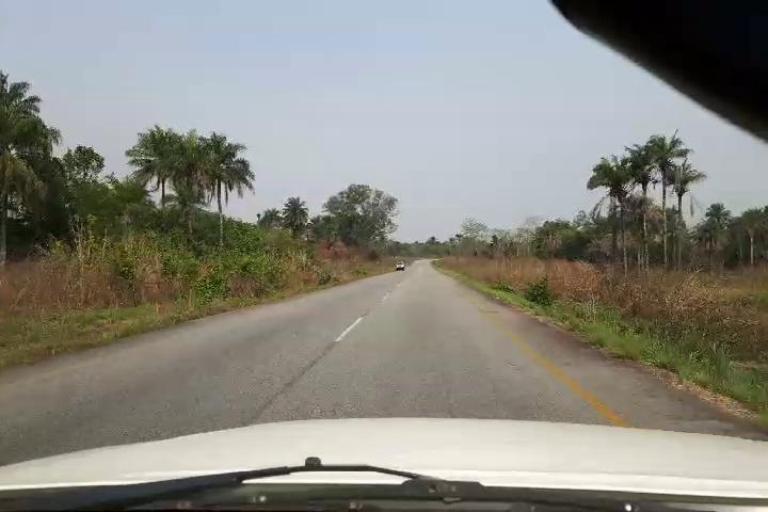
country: SL
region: Southern Province
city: Largo
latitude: 8.3061
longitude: -12.2053
